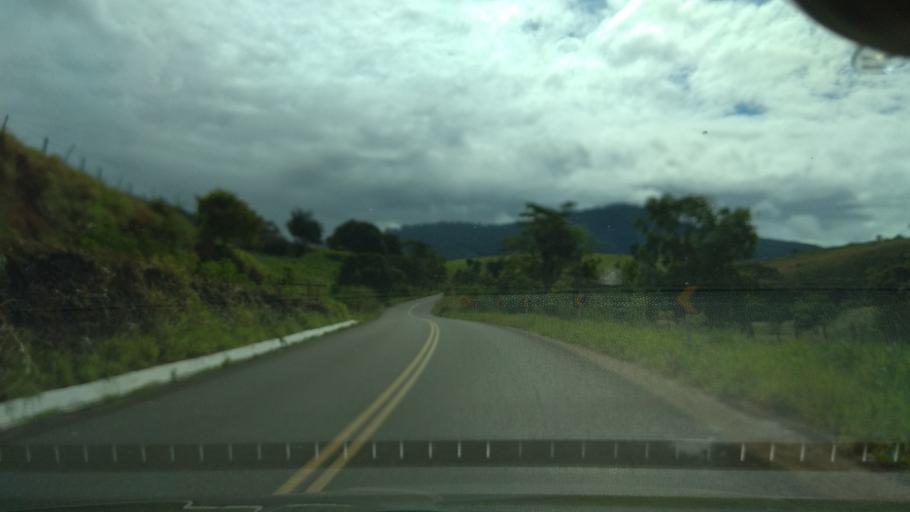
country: BR
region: Bahia
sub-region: Ubaira
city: Ubaira
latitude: -13.2622
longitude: -39.6779
